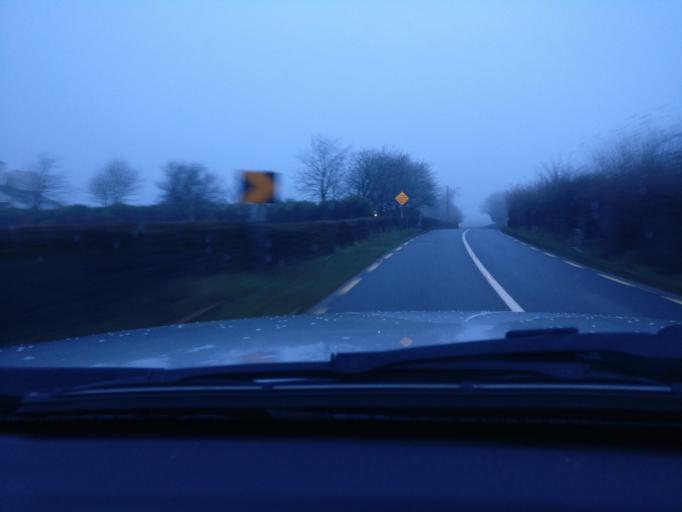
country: IE
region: Leinster
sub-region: An Mhi
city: Athboy
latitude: 53.6315
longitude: -6.8996
